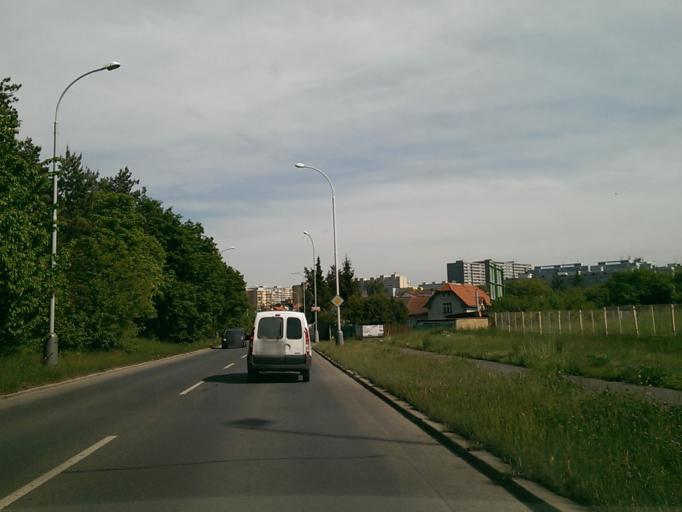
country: CZ
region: Central Bohemia
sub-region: Okres Praha-Zapad
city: Pruhonice
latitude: 50.0377
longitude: 14.5223
